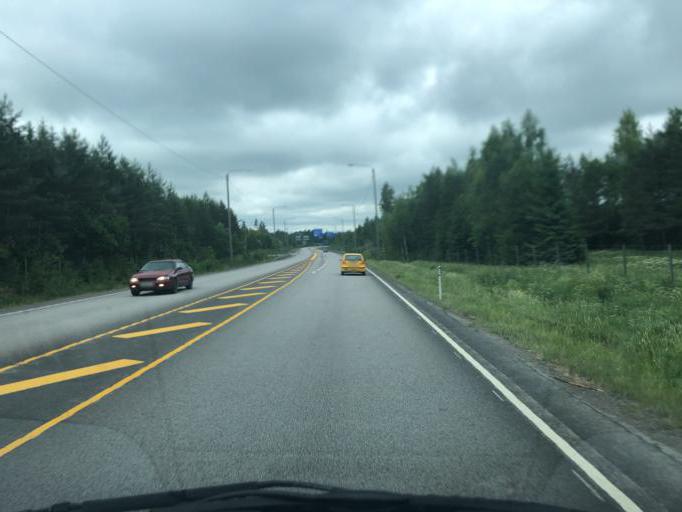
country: FI
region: Uusimaa
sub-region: Loviisa
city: Perna
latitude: 60.5124
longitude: 25.9652
